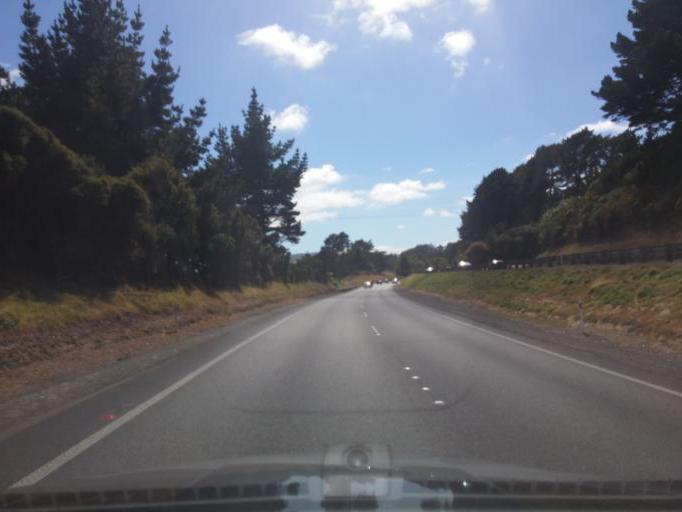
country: NZ
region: Wellington
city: Petone
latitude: -41.1975
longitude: 174.8247
